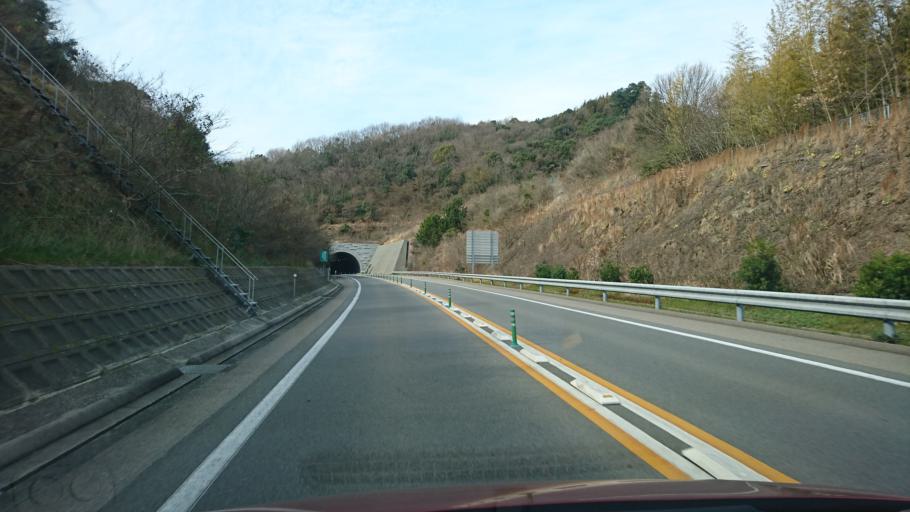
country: JP
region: Hiroshima
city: Innoshima
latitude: 34.1311
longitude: 133.0284
